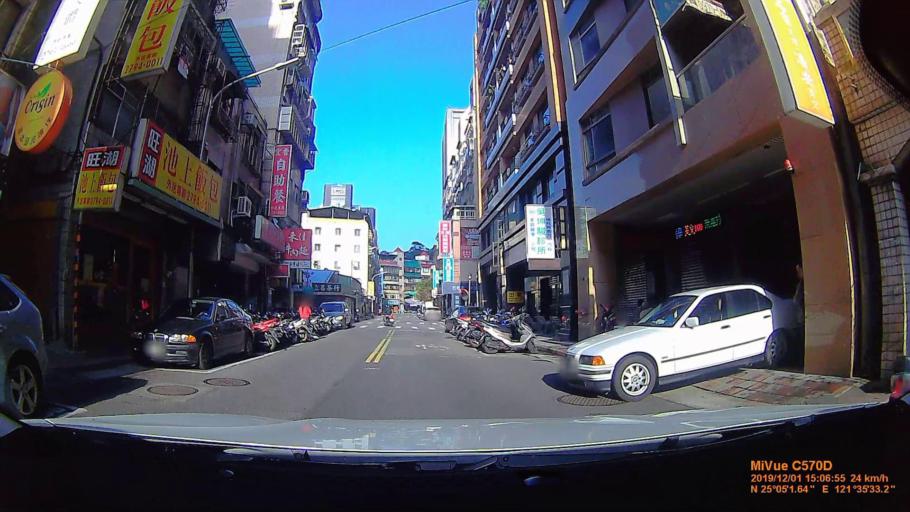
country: TW
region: Taipei
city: Taipei
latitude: 25.0838
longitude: 121.5926
